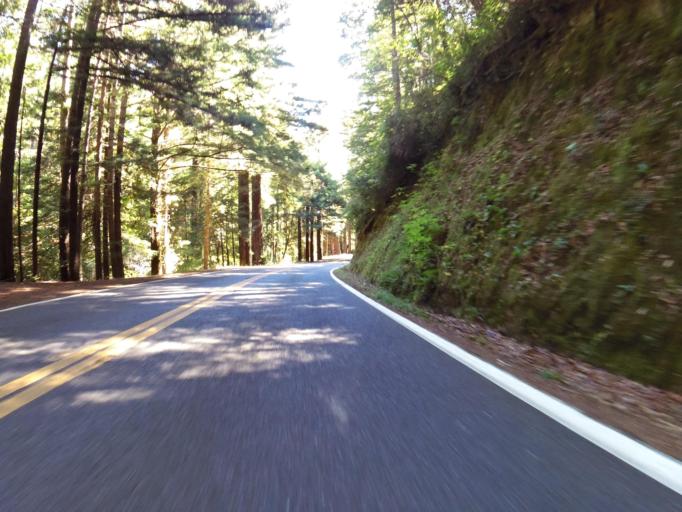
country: US
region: California
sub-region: Humboldt County
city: Redway
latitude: 39.8193
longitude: -123.7825
